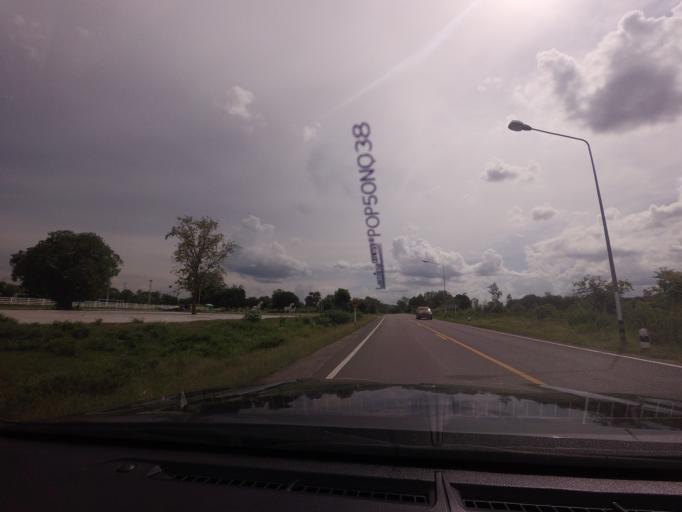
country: TH
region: Kanchanaburi
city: Bo Phloi
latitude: 14.1666
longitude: 99.4340
